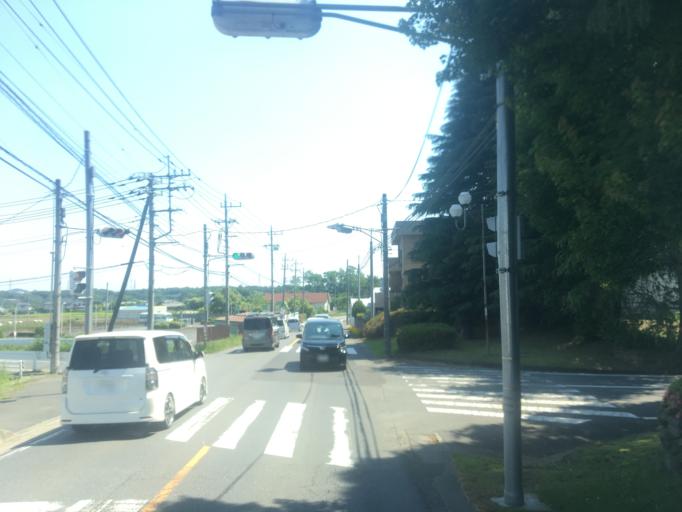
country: JP
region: Saitama
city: Ogawa
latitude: 36.0243
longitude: 139.3234
